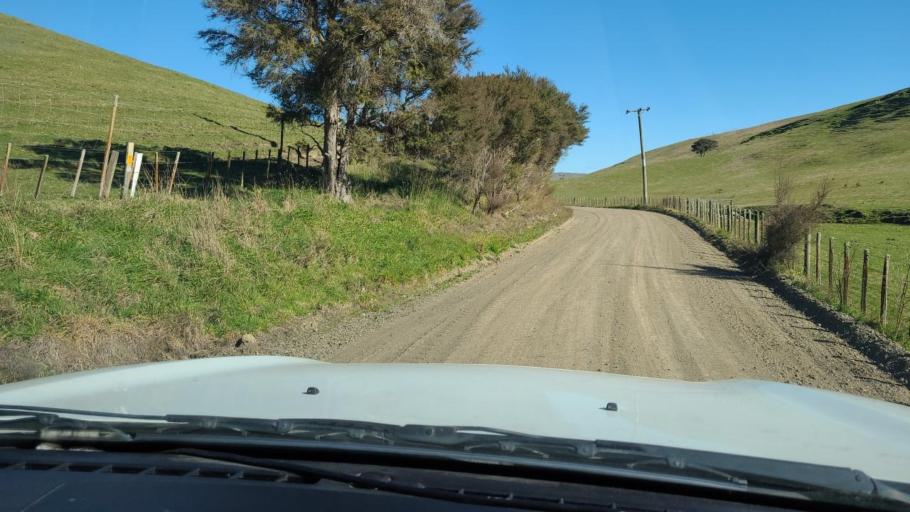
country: NZ
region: Hawke's Bay
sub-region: Napier City
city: Taradale
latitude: -39.4908
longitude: 176.4780
